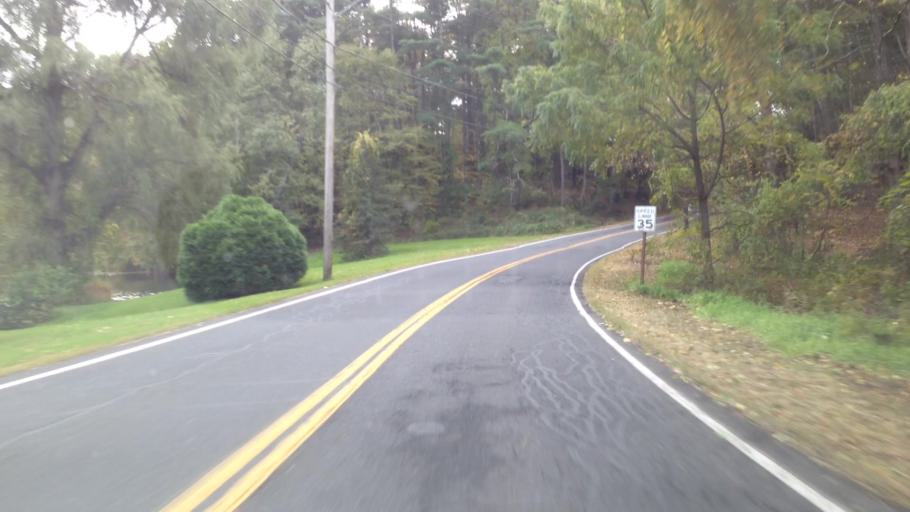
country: US
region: New York
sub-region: Ulster County
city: Tillson
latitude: 41.8348
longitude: -74.0779
